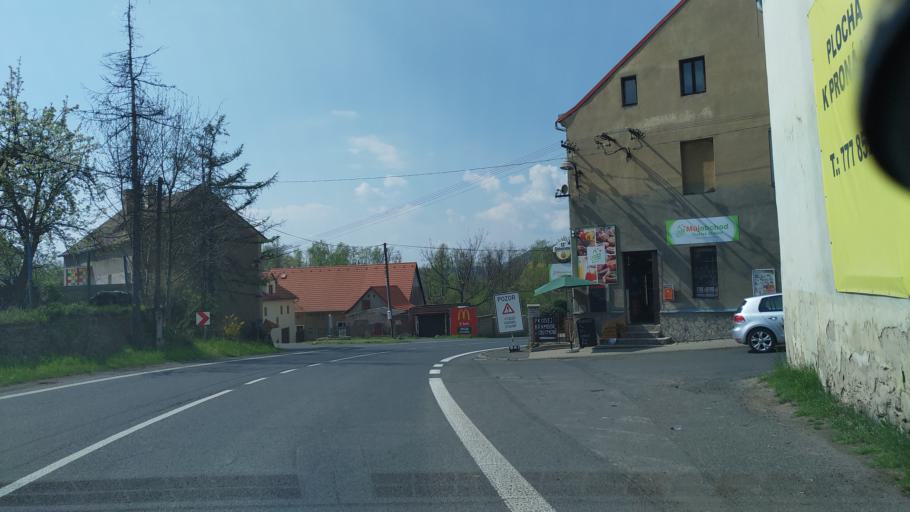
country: CZ
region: Ustecky
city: Krupka
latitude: 50.6721
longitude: 13.8941
